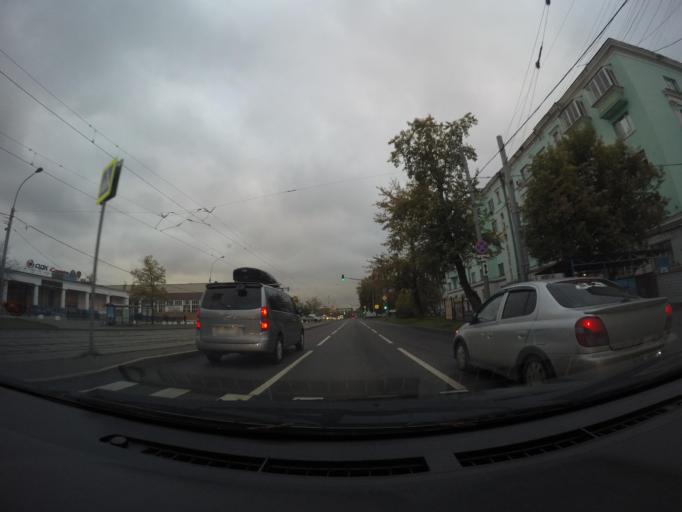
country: RU
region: Moscow
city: Lefortovo
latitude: 55.7736
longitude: 37.7251
